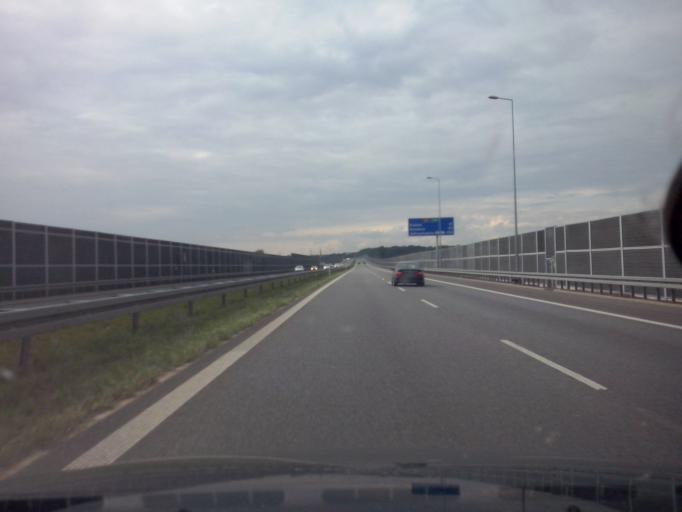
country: PL
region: Lesser Poland Voivodeship
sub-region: Powiat bochenski
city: Bochnia
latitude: 50.0032
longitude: 20.4429
